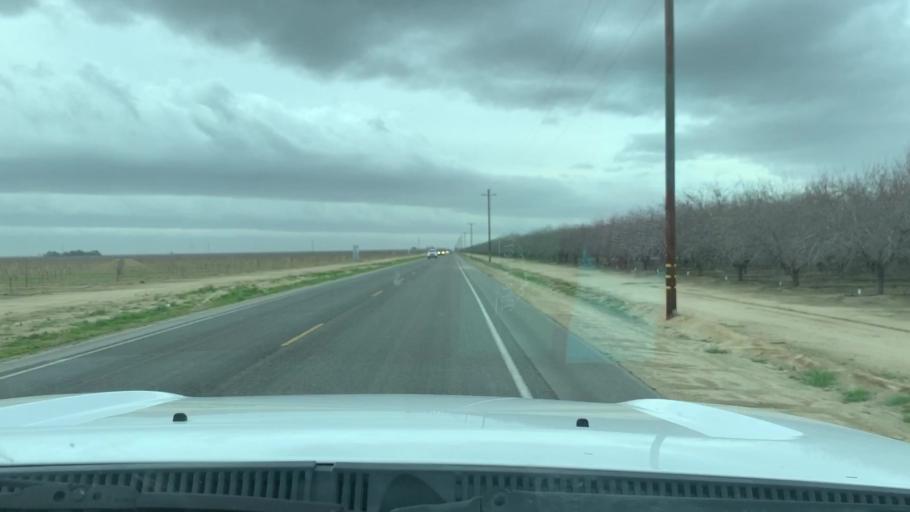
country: US
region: California
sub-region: Kern County
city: Wasco
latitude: 35.5581
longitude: -119.2984
